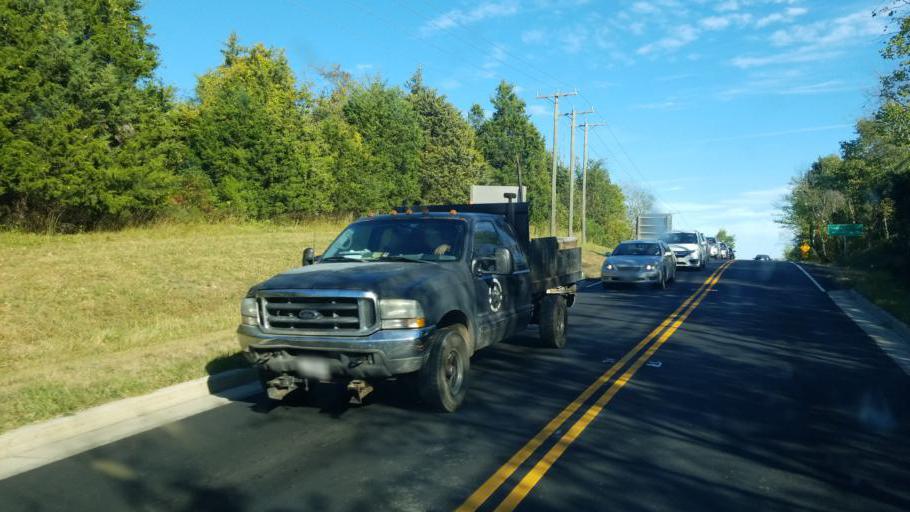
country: US
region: Virginia
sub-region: Prince William County
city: Bull Run Mountain Estates
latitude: 38.9685
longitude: -77.6210
